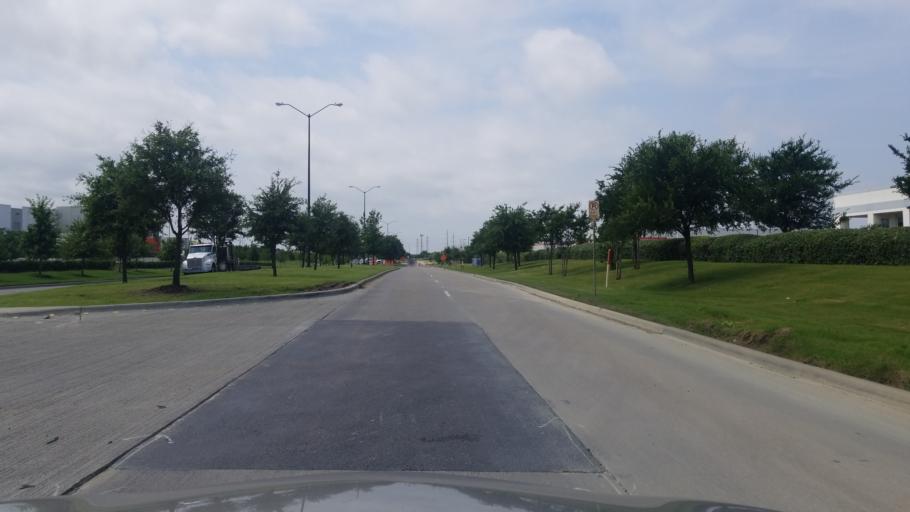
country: US
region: Texas
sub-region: Dallas County
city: Duncanville
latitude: 32.6771
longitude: -96.9670
